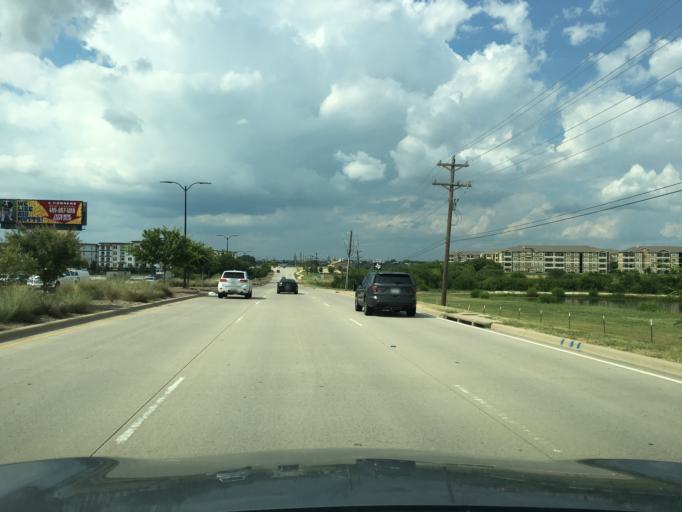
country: US
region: Texas
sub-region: Denton County
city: Little Elm
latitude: 33.1560
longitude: -96.8907
